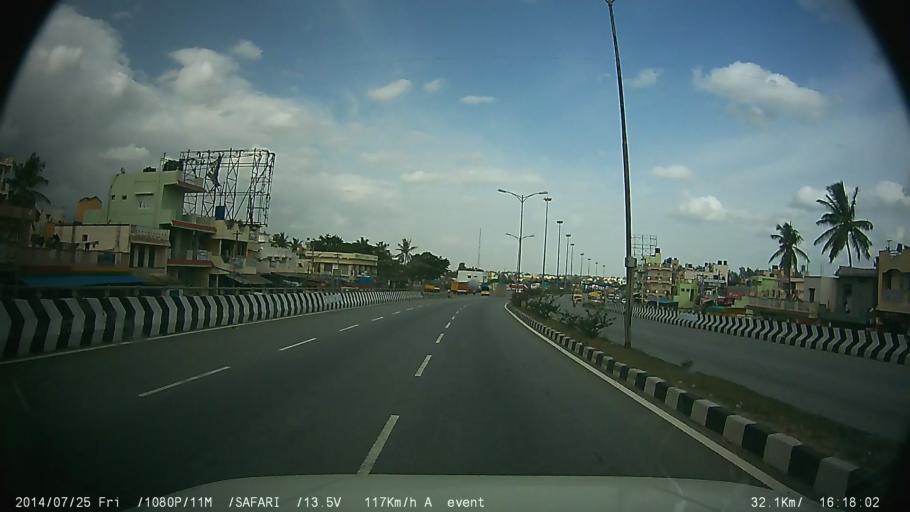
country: IN
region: Tamil Nadu
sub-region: Krishnagiri
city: Hosur
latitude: 12.7784
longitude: 77.7733
